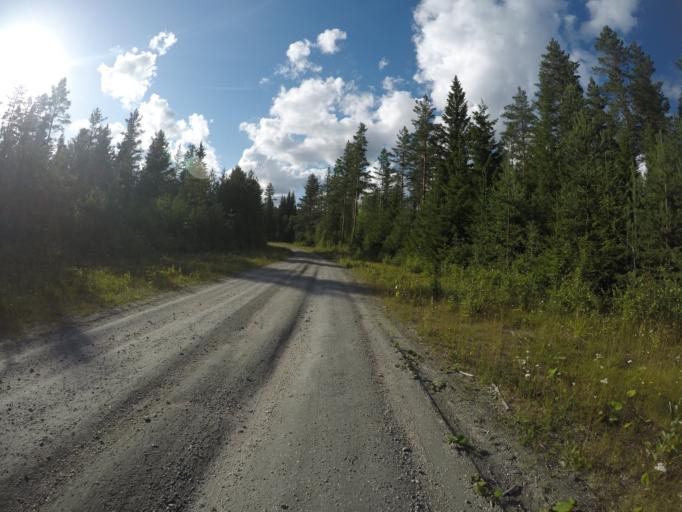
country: SE
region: OErebro
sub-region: Hallefors Kommun
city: Haellefors
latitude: 59.9856
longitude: 14.5406
